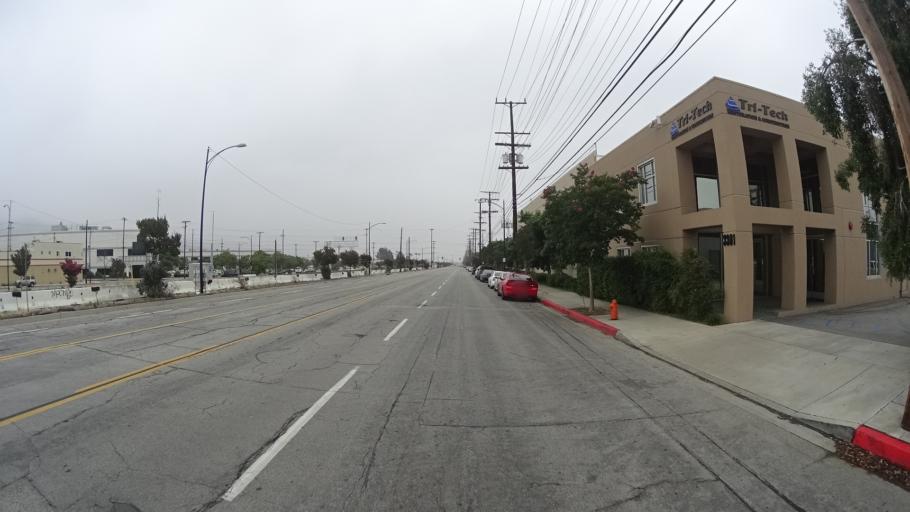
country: US
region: California
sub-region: Los Angeles County
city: Burbank
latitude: 34.2037
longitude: -118.3465
